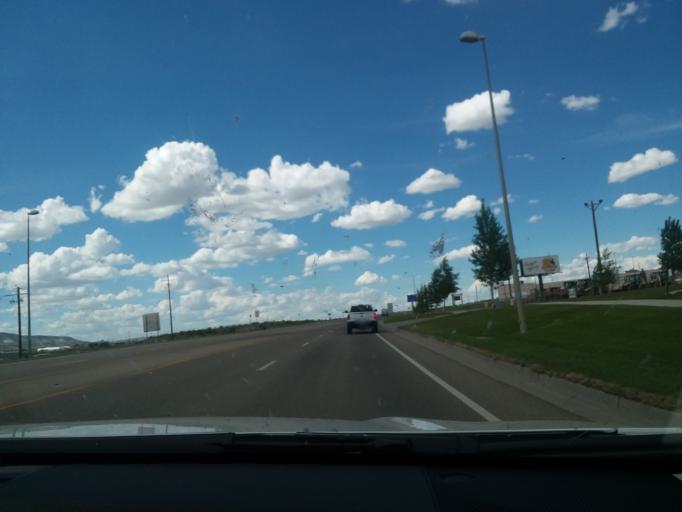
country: US
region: Wyoming
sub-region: Sweetwater County
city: North Rock Springs
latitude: 41.6217
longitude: -109.2331
